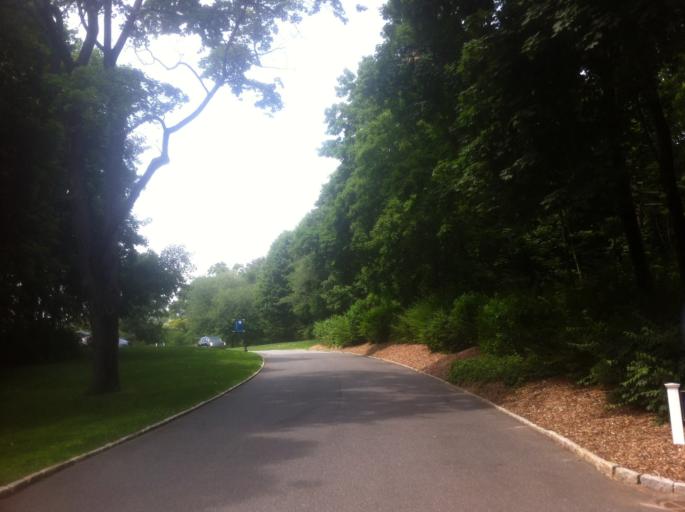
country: US
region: New York
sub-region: Nassau County
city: Locust Valley
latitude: 40.8756
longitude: -73.5762
